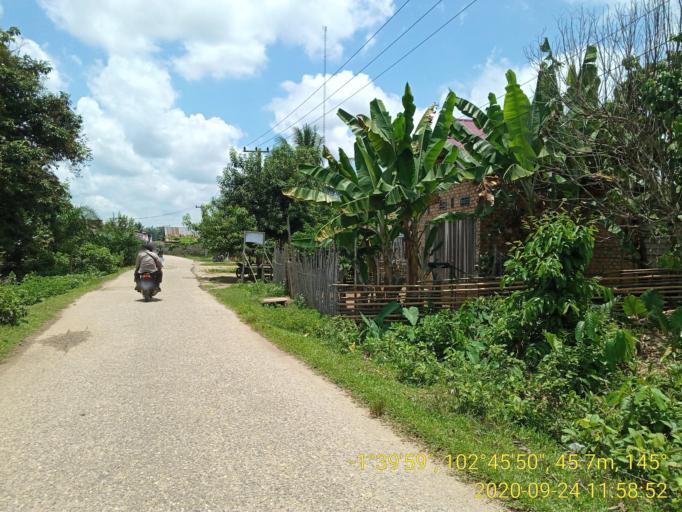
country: ID
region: Jambi
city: Sungaibengkal
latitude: -1.6665
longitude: 102.7639
